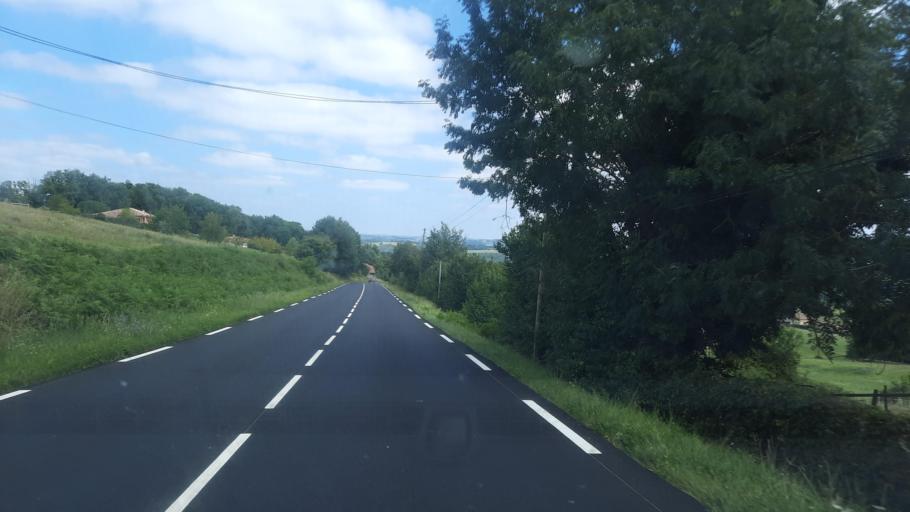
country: FR
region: Midi-Pyrenees
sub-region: Departement de la Haute-Garonne
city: Boulogne-sur-Gesse
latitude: 43.2995
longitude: 0.5976
